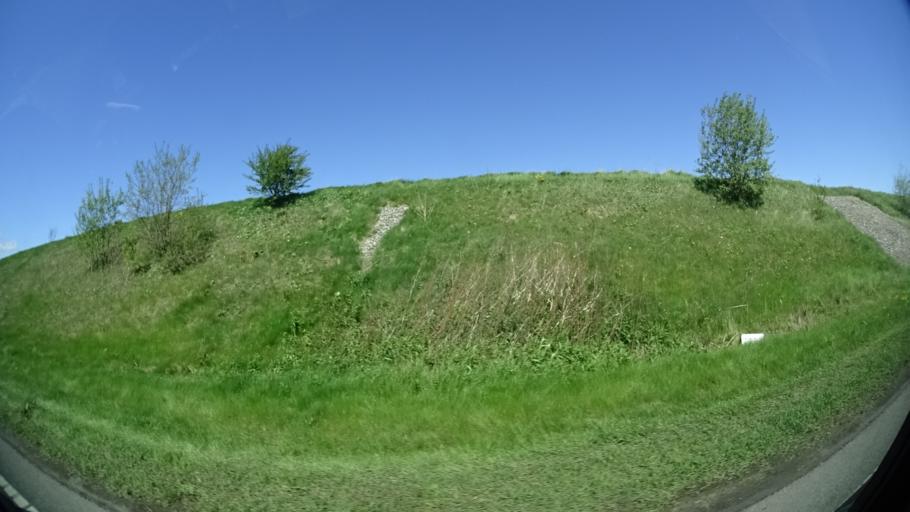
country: DK
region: Central Jutland
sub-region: Arhus Kommune
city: Kolt
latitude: 56.1213
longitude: 10.0721
